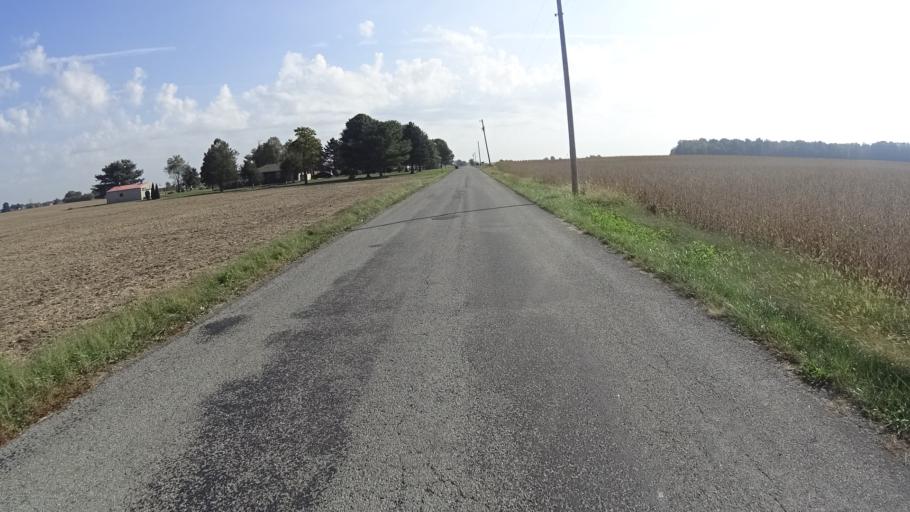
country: US
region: Indiana
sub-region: Madison County
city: Lapel
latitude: 40.0455
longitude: -85.8617
